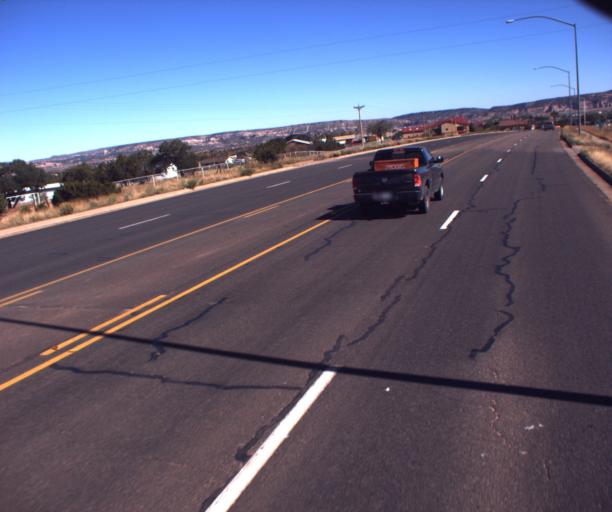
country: US
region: Arizona
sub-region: Apache County
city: Saint Michaels
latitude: 35.6592
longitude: -109.1179
